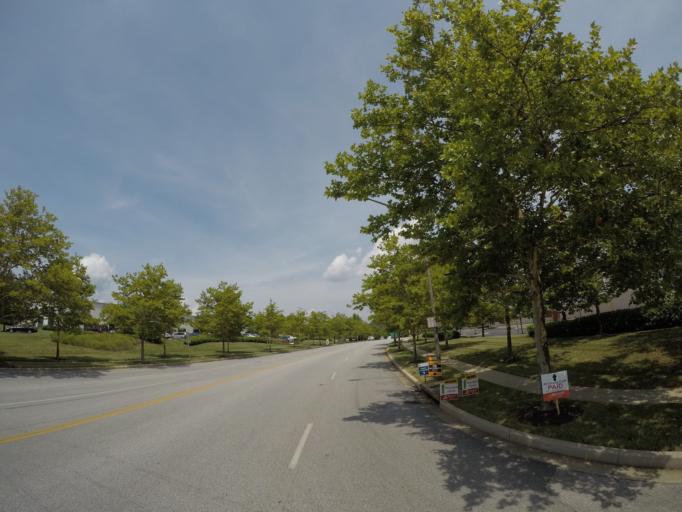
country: US
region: Maryland
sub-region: Howard County
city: Savage
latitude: 39.1314
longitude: -76.8204
